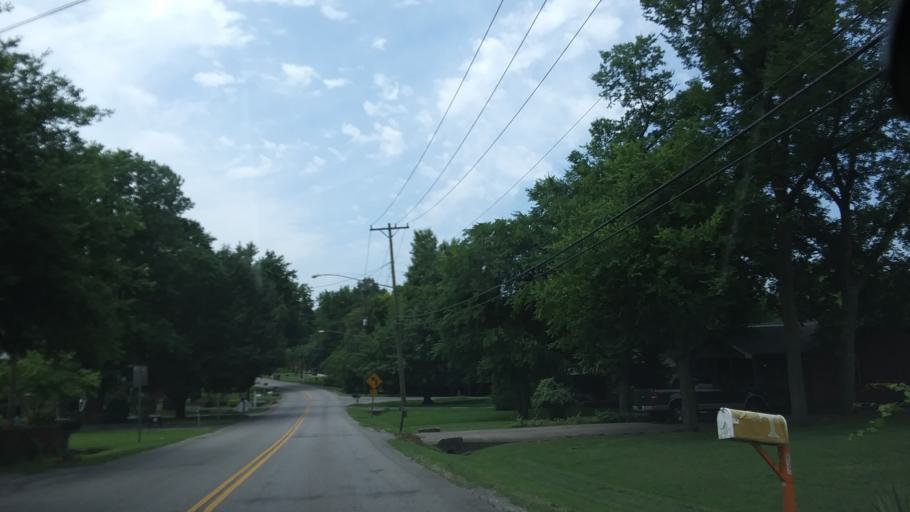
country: US
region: Tennessee
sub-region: Davidson County
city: Belle Meade
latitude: 36.1555
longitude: -86.8778
